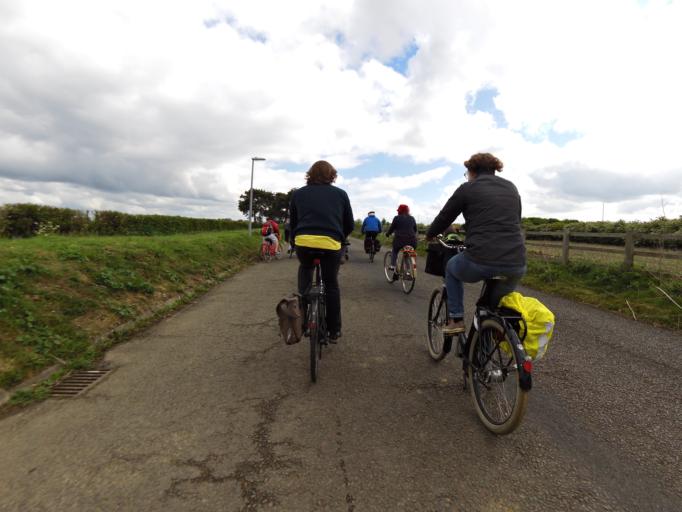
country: GB
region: England
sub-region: Cambridgeshire
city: Fulbourn
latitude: 52.2146
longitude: 0.2132
